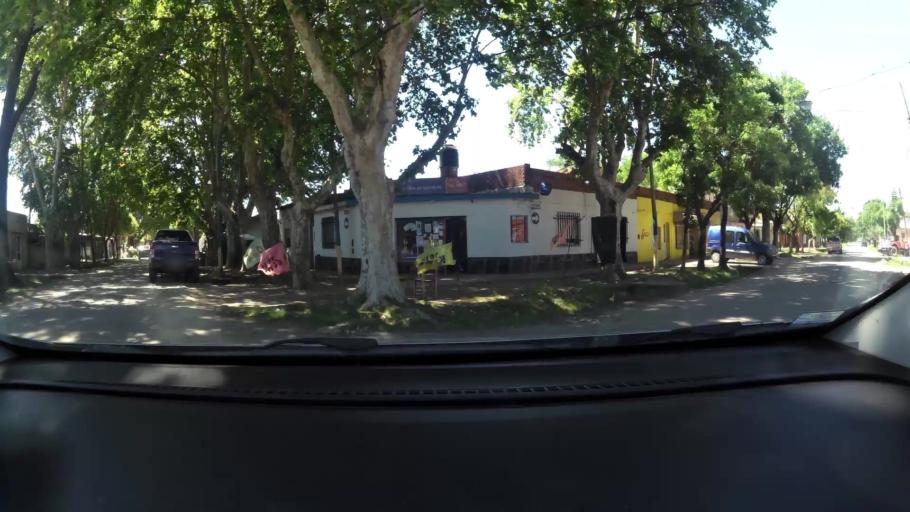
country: AR
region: Santa Fe
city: Perez
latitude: -32.9536
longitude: -60.7201
